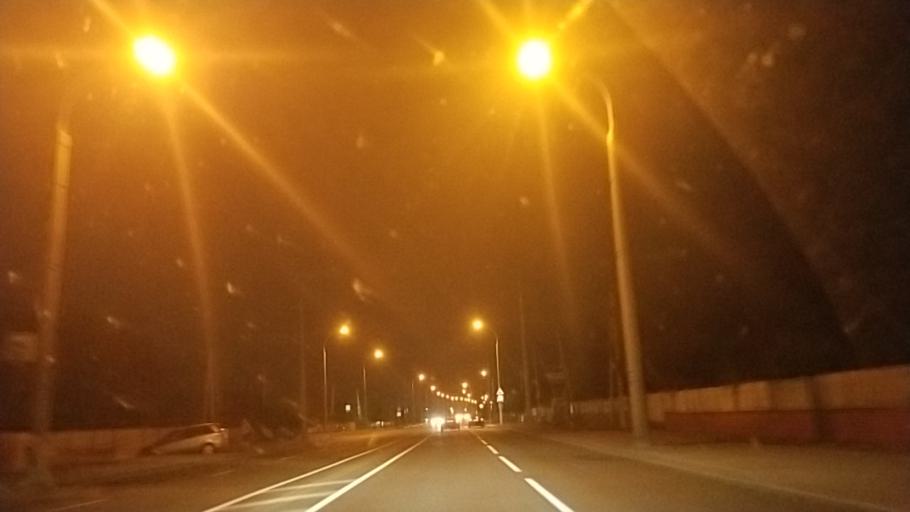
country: BY
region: Brest
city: Brest
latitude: 52.0652
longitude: 23.7384
